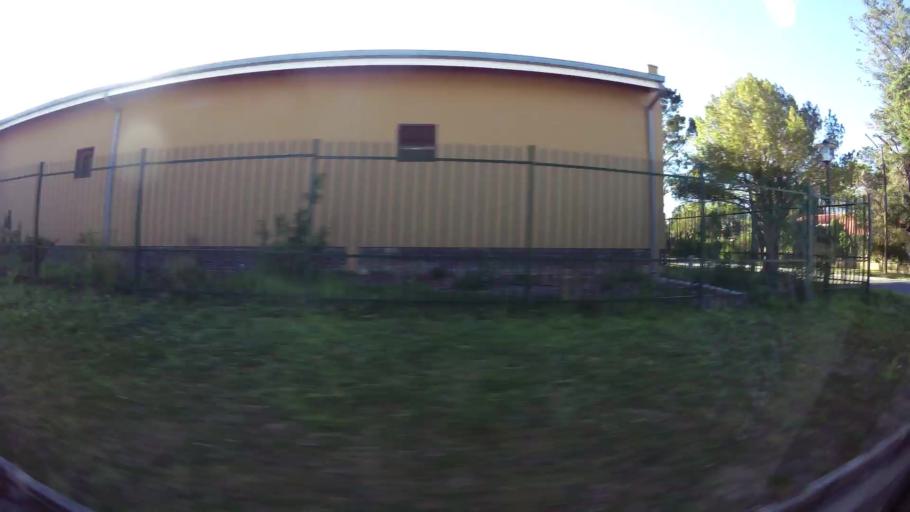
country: ZA
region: Western Cape
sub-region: Eden District Municipality
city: George
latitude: -33.9492
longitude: 22.4512
